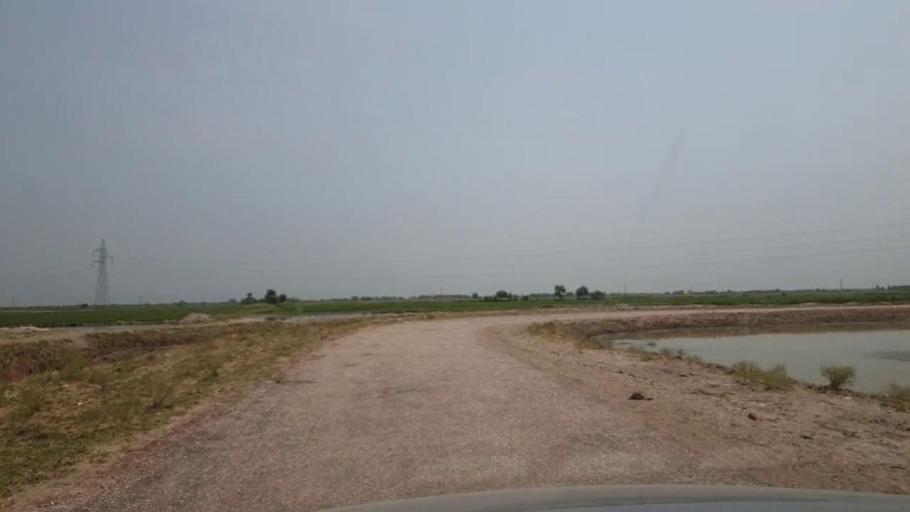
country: PK
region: Sindh
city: Garhi Yasin
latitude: 27.8897
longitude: 68.4938
